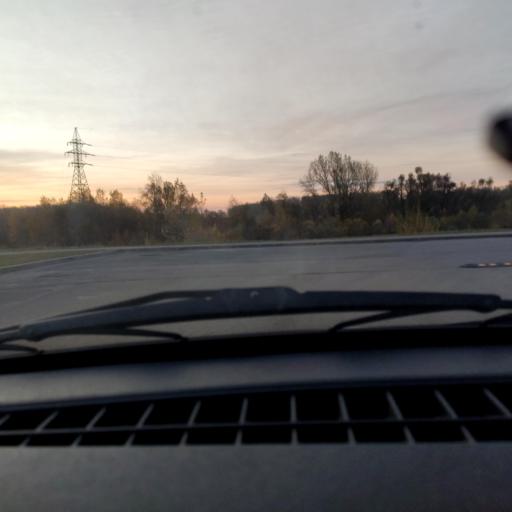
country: RU
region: Bashkortostan
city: Ufa
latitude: 54.7902
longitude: 56.0824
